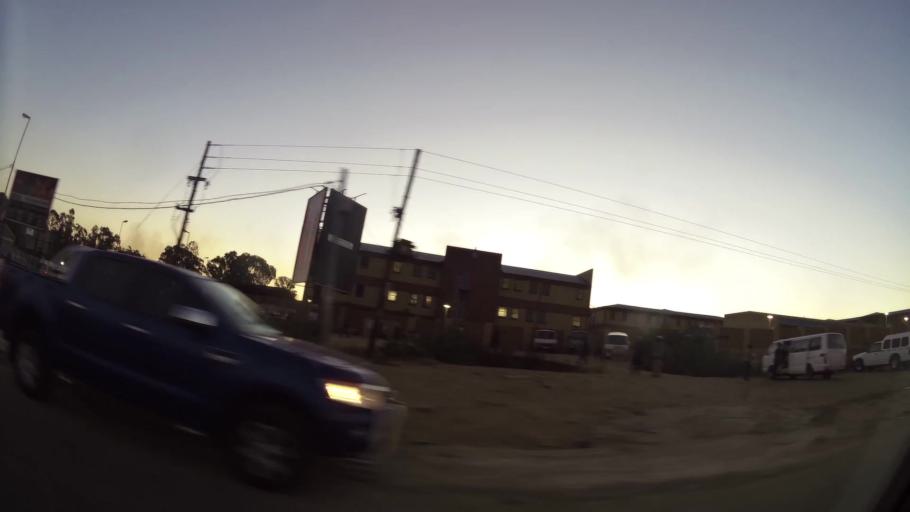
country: ZA
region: Gauteng
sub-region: City of Johannesburg Metropolitan Municipality
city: Diepsloot
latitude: -25.9226
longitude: 28.0228
